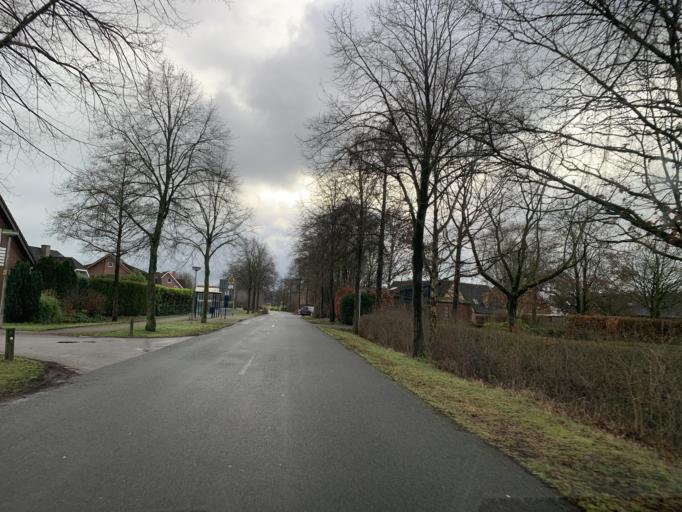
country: DE
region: North Rhine-Westphalia
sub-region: Regierungsbezirk Munster
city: Senden
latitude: 51.9213
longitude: 7.4736
